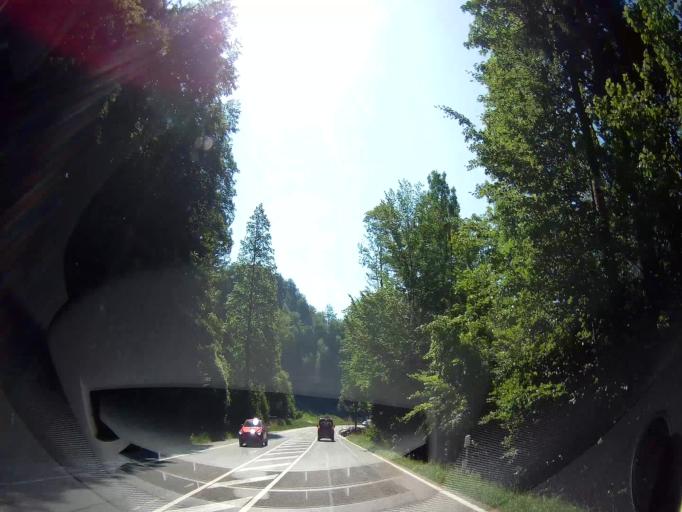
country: DE
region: Bavaria
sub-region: Upper Bavaria
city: Marktschellenberg
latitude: 47.6577
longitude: 13.0396
